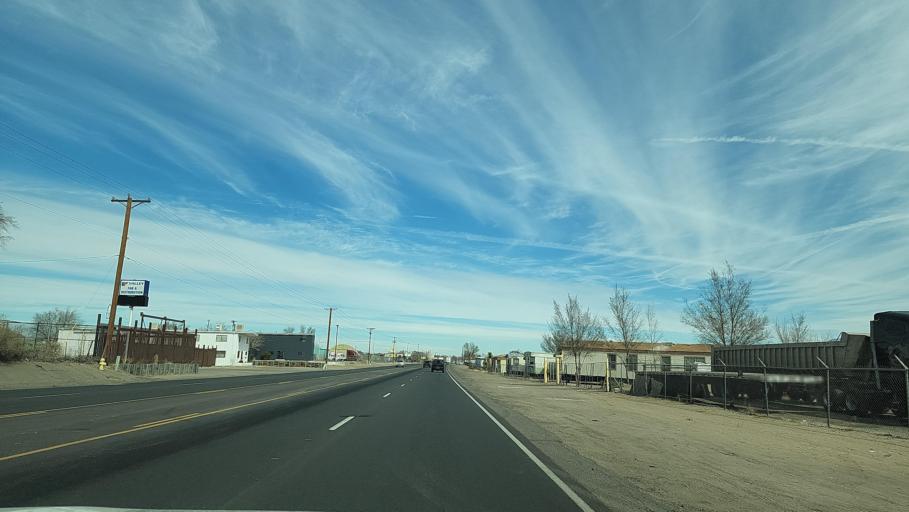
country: US
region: New Mexico
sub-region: Bernalillo County
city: South Valley
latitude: 35.0388
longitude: -106.7117
